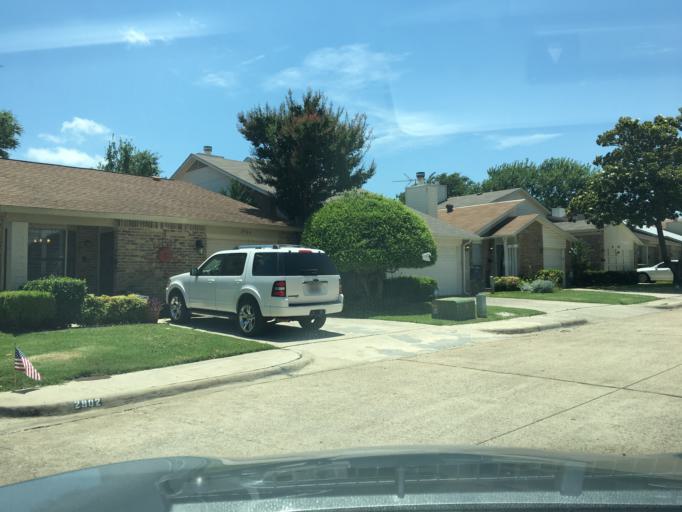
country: US
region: Texas
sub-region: Dallas County
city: Garland
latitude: 32.9482
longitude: -96.6710
